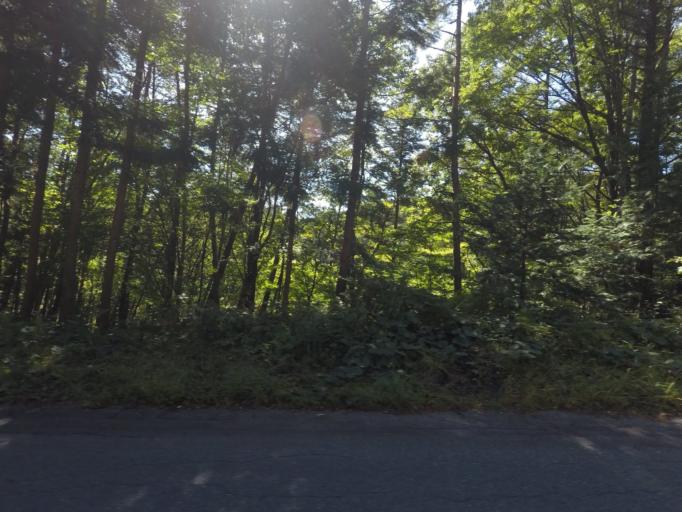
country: JP
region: Nagano
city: Ina
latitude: 35.9646
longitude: 137.7473
